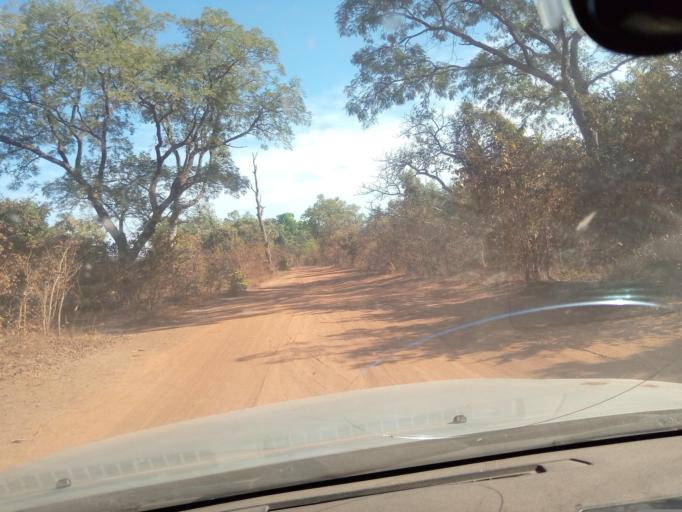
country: ML
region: Sikasso
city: Sikasso
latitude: 11.4699
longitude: -5.3285
